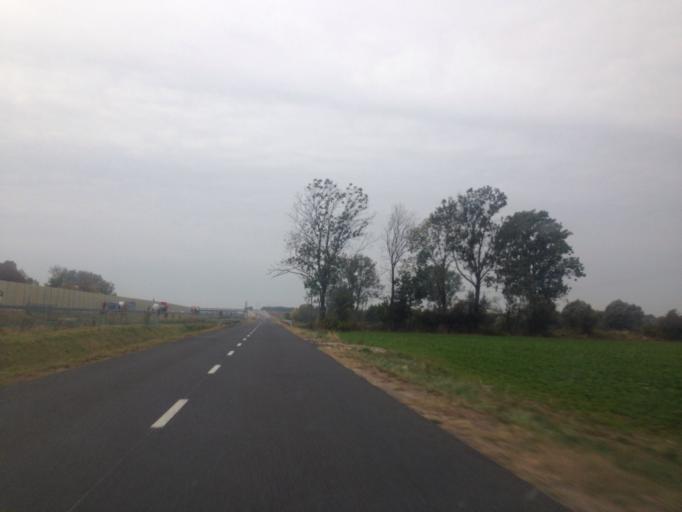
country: PL
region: Greater Poland Voivodeship
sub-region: Powiat gnieznienski
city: Lubowo
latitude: 52.4779
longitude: 17.4140
